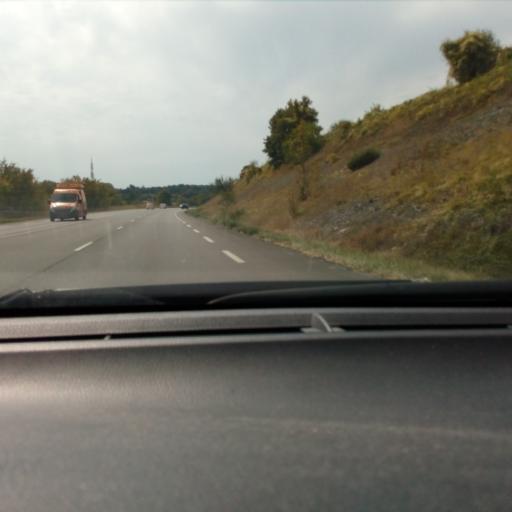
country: FR
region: Poitou-Charentes
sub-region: Departement de la Charente
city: Saint-Saturnin
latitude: 45.6731
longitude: 0.0428
